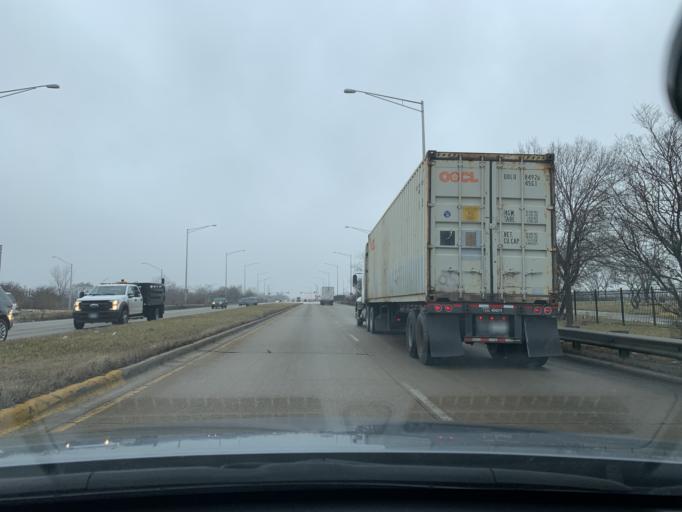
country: US
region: Illinois
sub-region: Cook County
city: Alsip
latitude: 41.6619
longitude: -87.7340
